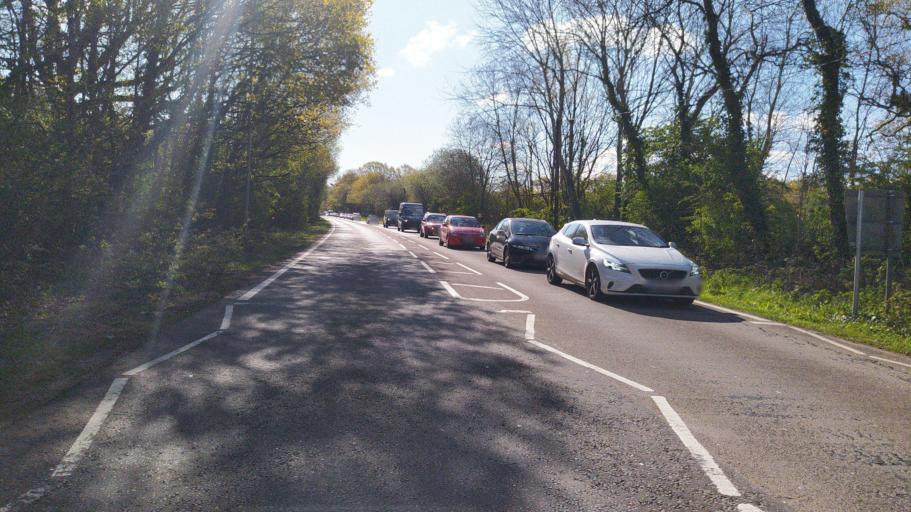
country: GB
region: England
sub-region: Hampshire
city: Marchwood
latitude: 50.8851
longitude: -1.4556
